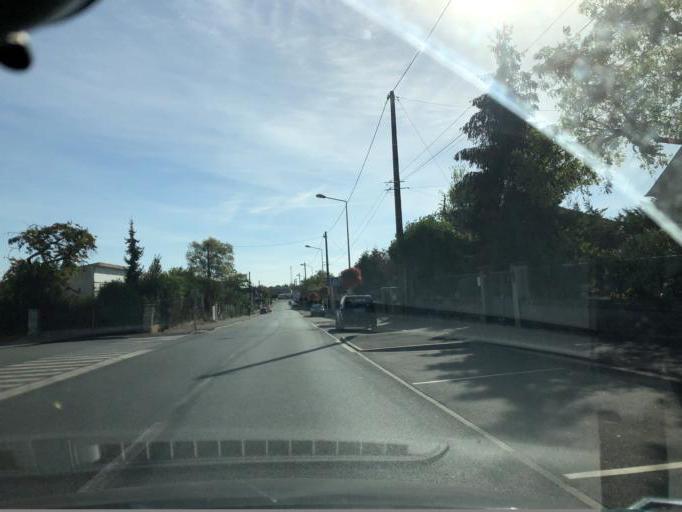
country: FR
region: Centre
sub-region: Departement du Loiret
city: Malesherbes
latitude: 48.2961
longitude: 2.3930
